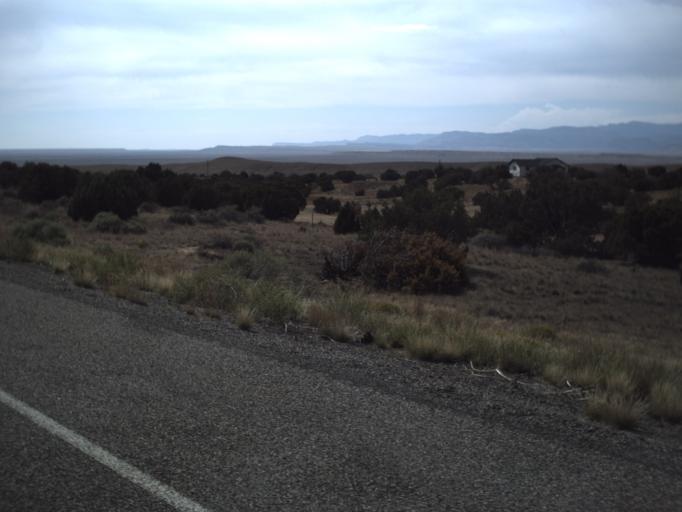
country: US
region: Colorado
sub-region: Mesa County
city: Loma
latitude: 39.1709
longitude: -109.1316
